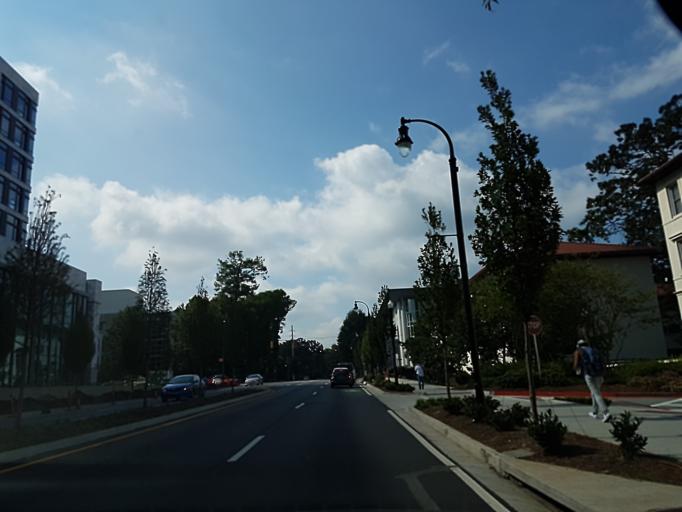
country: US
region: Georgia
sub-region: DeKalb County
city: North Decatur
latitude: 33.7914
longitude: -84.3210
